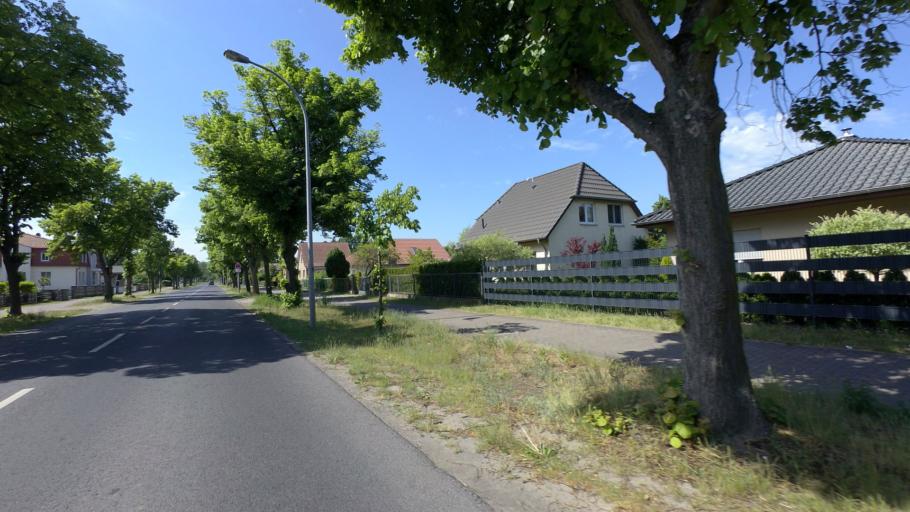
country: DE
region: Brandenburg
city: Oranienburg
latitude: 52.7318
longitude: 13.2428
